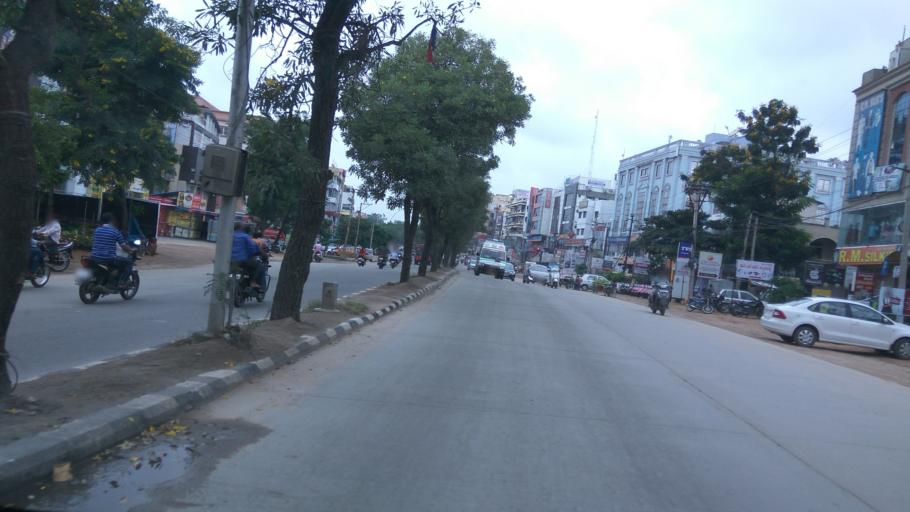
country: IN
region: Telangana
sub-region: Rangareddi
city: Secunderabad
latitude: 17.4808
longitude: 78.5562
